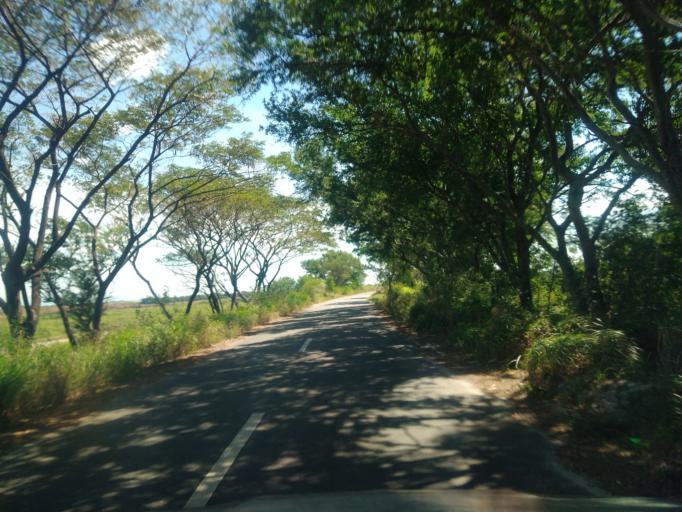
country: PH
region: Central Luzon
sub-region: Province of Pampanga
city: Balas
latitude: 15.0490
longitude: 120.5888
